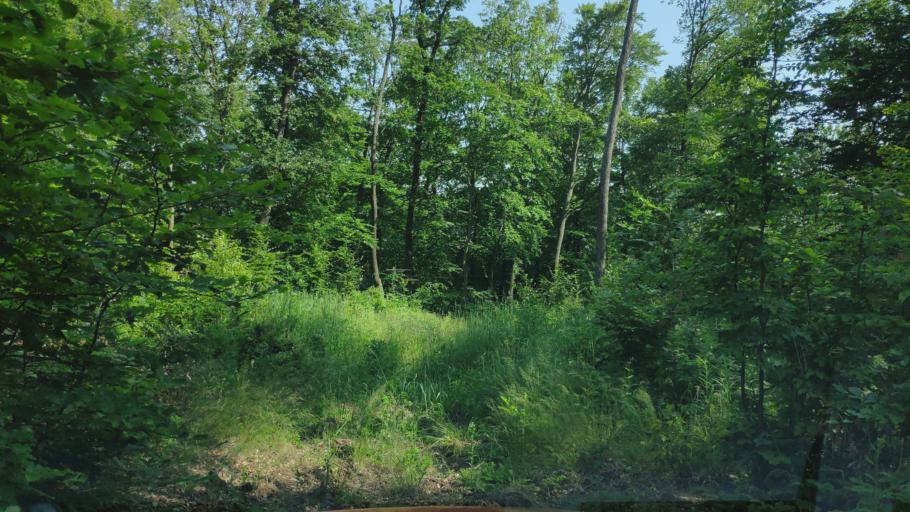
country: SK
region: Presovsky
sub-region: Okres Presov
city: Presov
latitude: 48.9685
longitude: 21.1525
